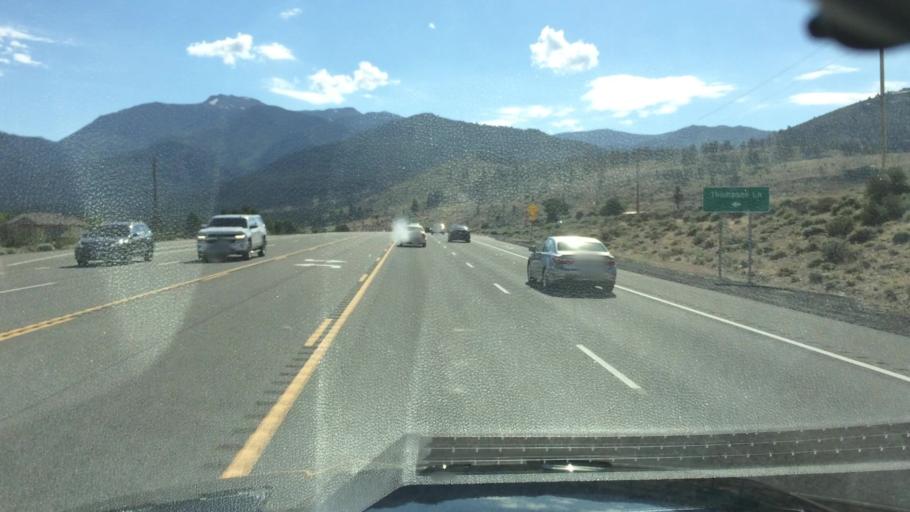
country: US
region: Nevada
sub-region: Washoe County
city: Reno
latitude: 39.3790
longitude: -119.8276
